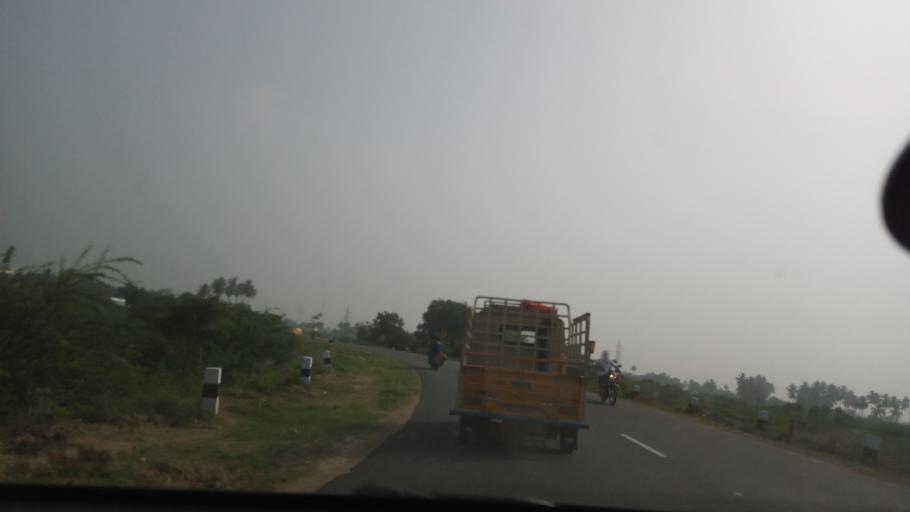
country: IN
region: Tamil Nadu
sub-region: Erode
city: Punjai Puliyampatti
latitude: 11.3958
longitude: 77.1815
